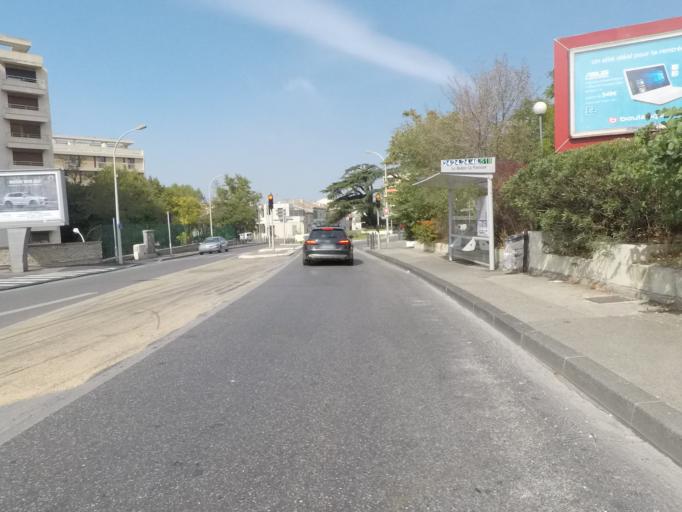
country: FR
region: Provence-Alpes-Cote d'Azur
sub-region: Departement des Bouches-du-Rhone
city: Marseille 09
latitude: 43.2566
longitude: 5.4196
